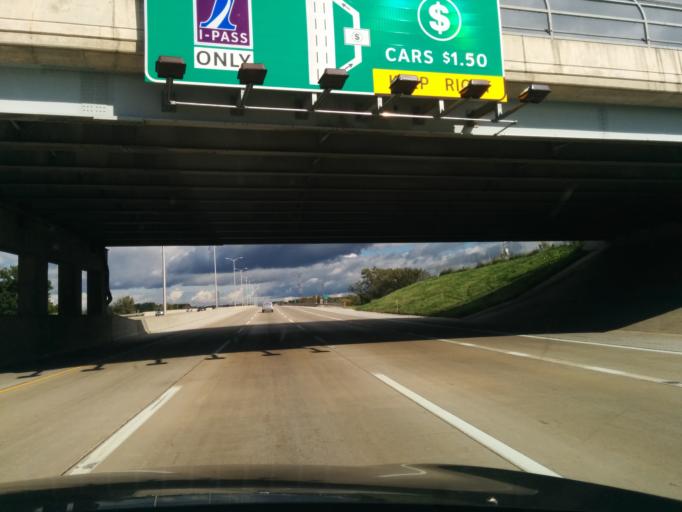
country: US
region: Illinois
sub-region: Kane County
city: North Aurora
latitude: 41.7959
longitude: -88.3244
